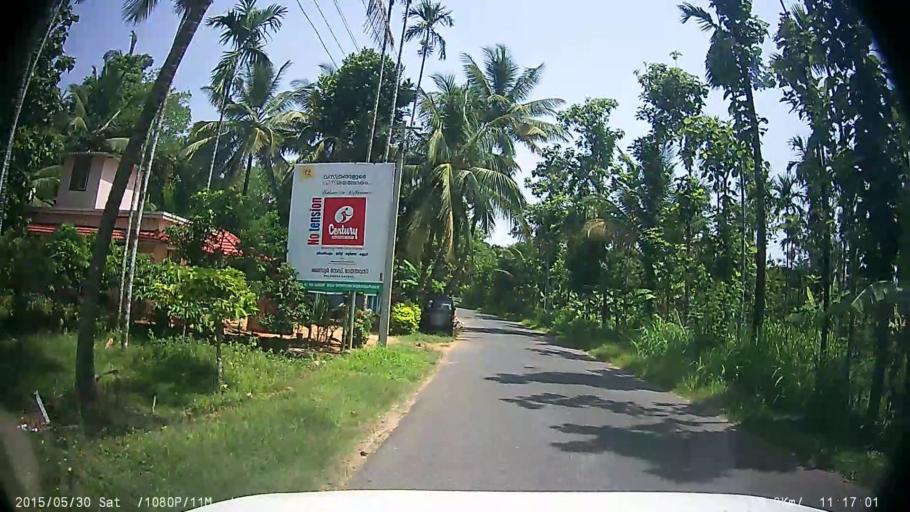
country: IN
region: Kerala
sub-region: Wayanad
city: Panamaram
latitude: 11.7763
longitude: 76.0523
